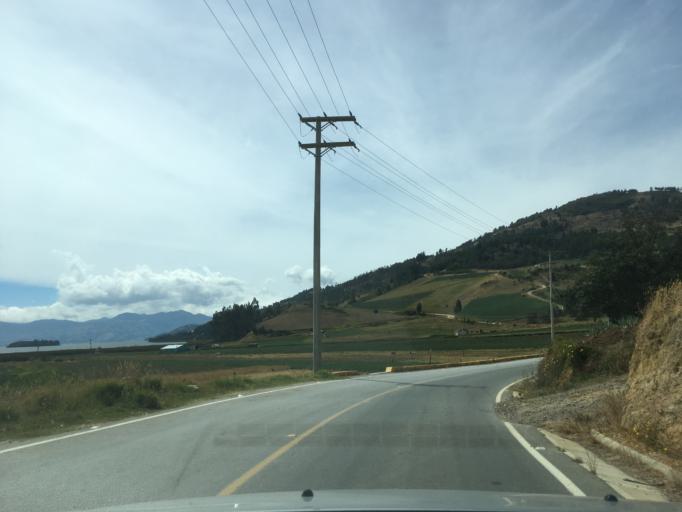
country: CO
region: Boyaca
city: Aquitania
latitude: 5.5981
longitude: -72.9141
